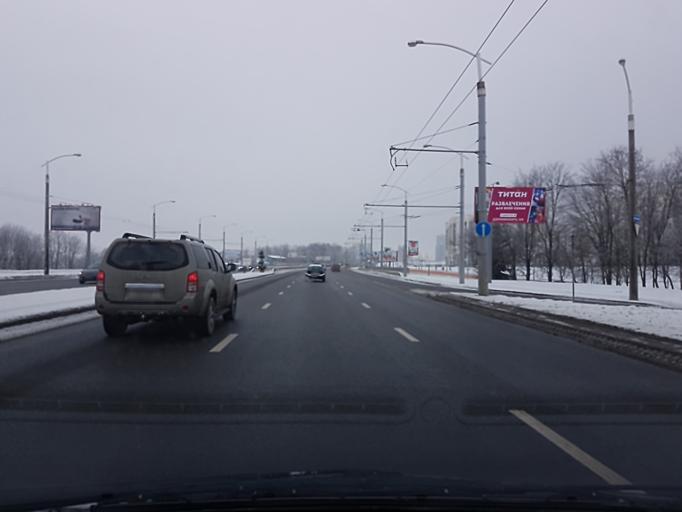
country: BY
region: Minsk
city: Novoye Medvezhino
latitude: 53.8722
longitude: 27.4938
